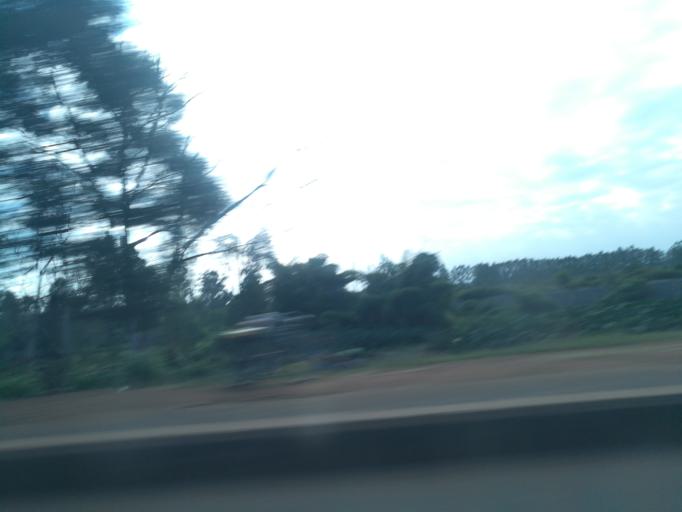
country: KE
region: Nairobi Area
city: Thika
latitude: -1.1131
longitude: 37.0117
